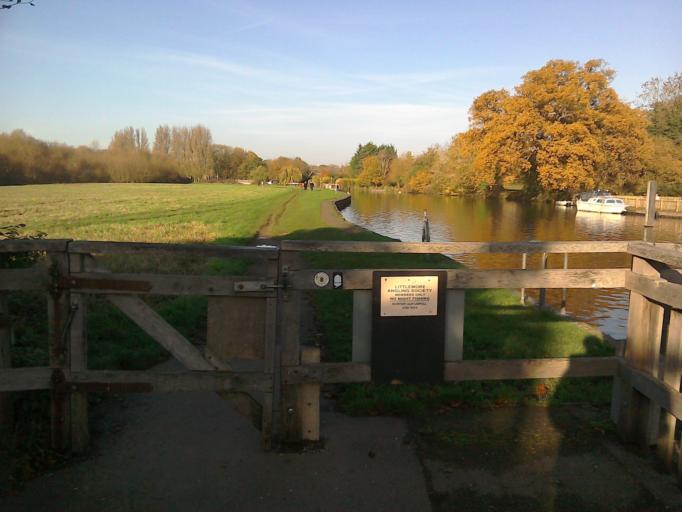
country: GB
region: England
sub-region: Oxfordshire
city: Radley
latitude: 51.7086
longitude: -1.2331
